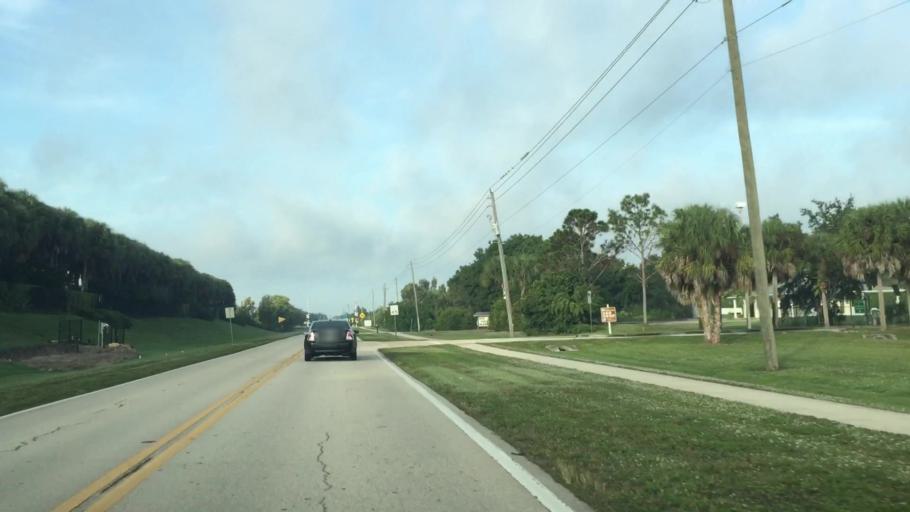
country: US
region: Florida
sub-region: Lee County
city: Estero
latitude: 26.4204
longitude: -81.8020
